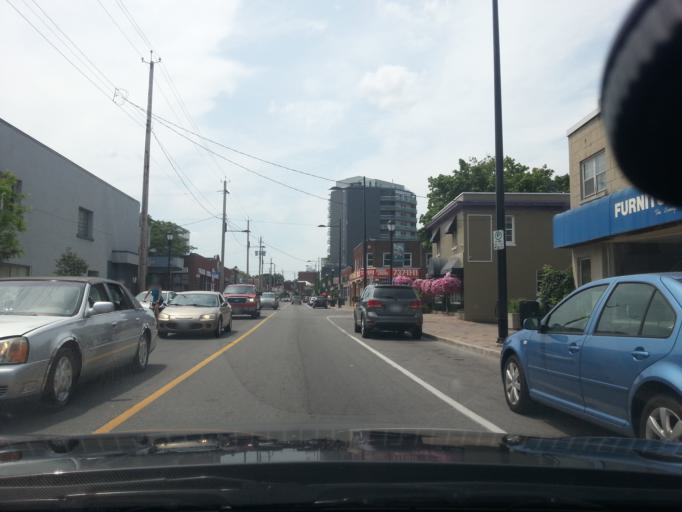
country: CA
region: Ontario
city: Ottawa
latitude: 45.4007
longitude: -75.7295
